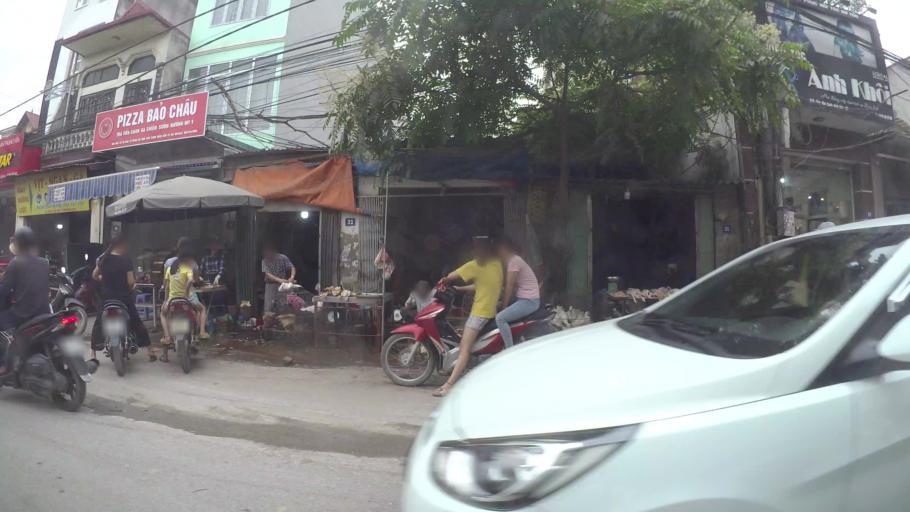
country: VN
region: Ha Noi
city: Cau Dien
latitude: 21.0348
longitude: 105.7377
